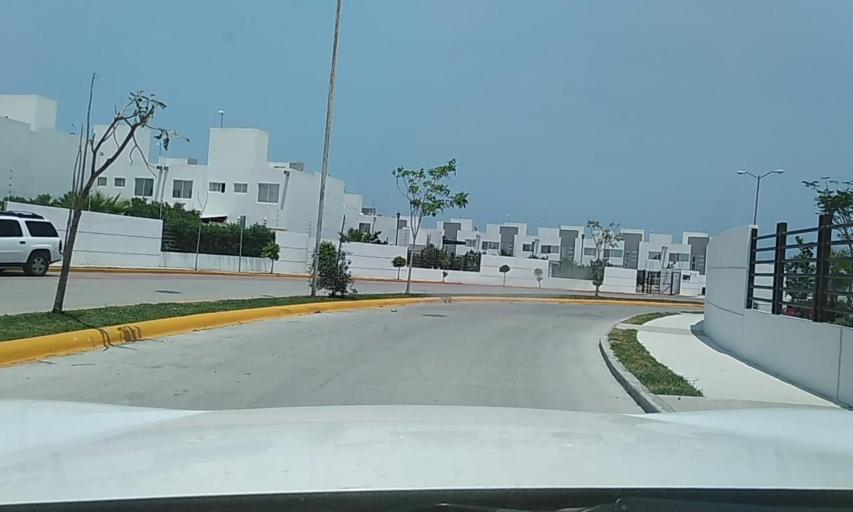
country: MX
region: Veracruz
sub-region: Veracruz
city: Hacienda Sotavento
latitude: 19.1237
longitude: -96.1699
